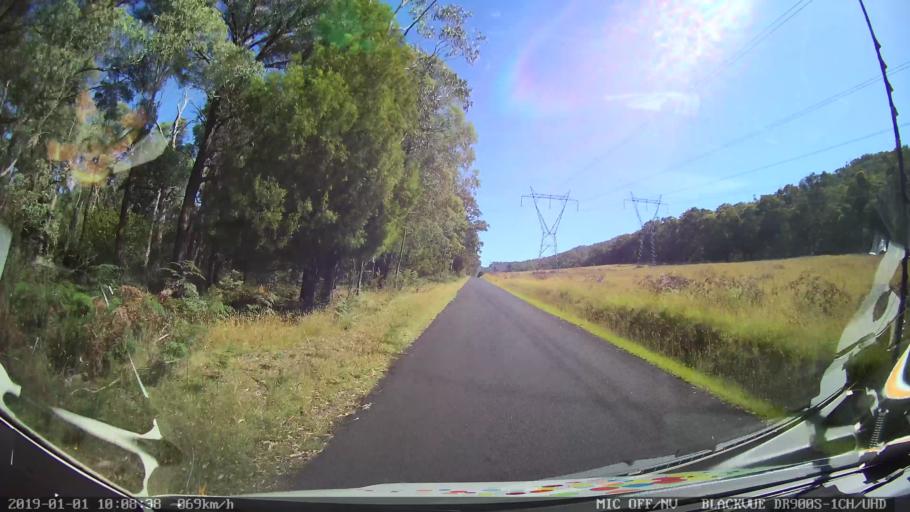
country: AU
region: New South Wales
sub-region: Snowy River
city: Jindabyne
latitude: -36.1573
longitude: 148.1577
